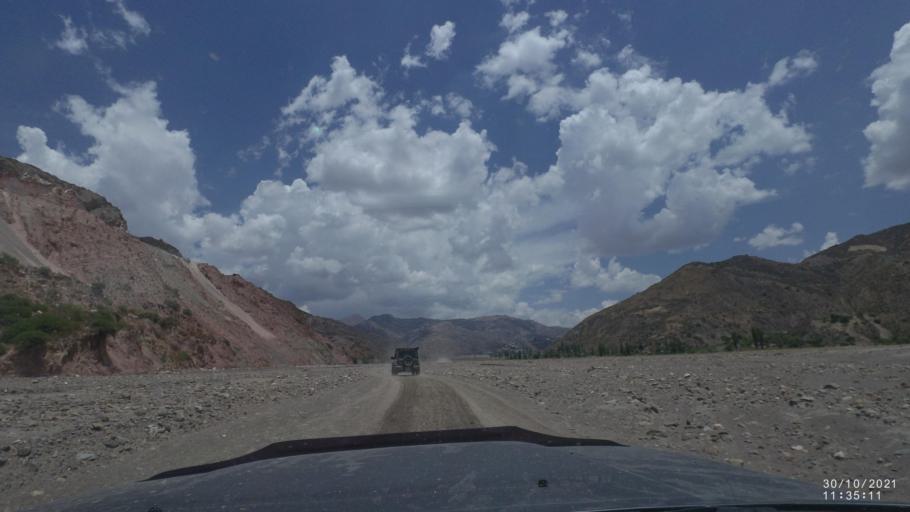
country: BO
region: Cochabamba
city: Sipe Sipe
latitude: -17.5239
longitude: -66.5972
